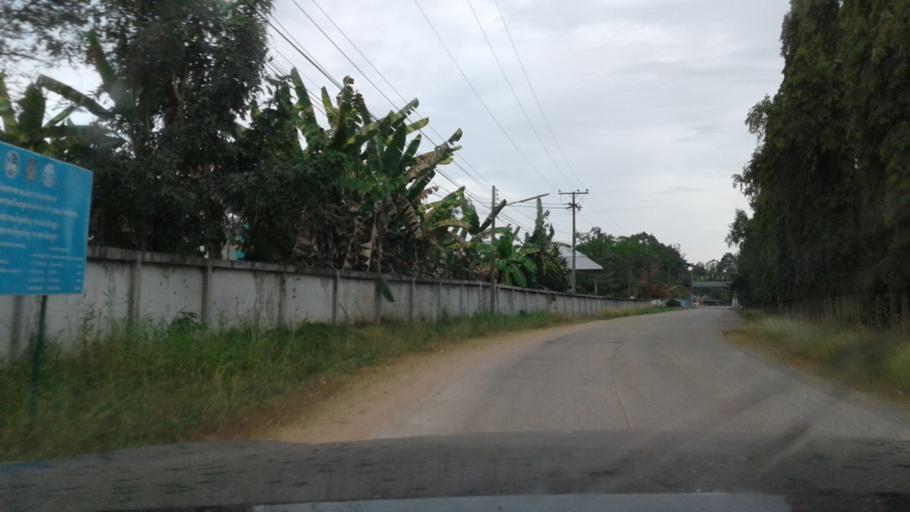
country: TH
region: Changwat Udon Thani
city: Nong Wua So
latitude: 17.2426
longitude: 102.5353
